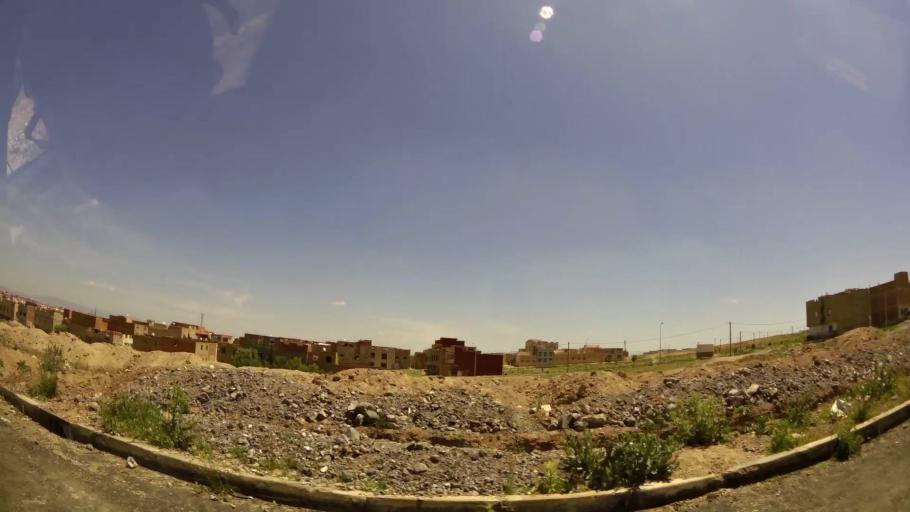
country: MA
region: Oriental
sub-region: Oujda-Angad
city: Oujda
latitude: 34.6529
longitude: -1.9518
